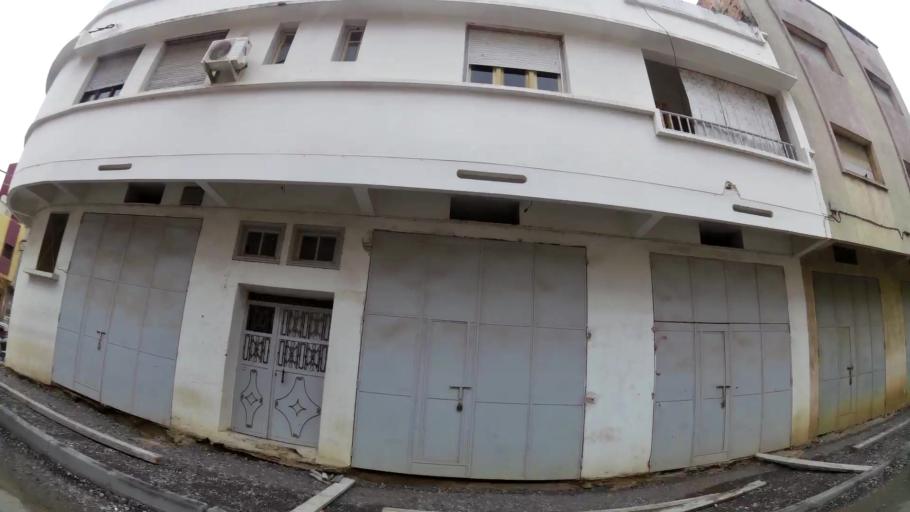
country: MA
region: Rabat-Sale-Zemmour-Zaer
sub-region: Khemisset
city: Tiflet
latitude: 33.8901
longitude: -6.3181
